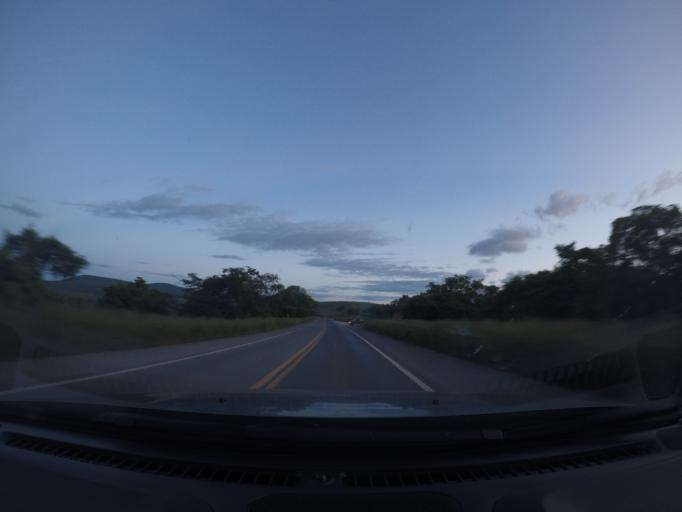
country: BR
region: Bahia
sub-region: Seabra
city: Seabra
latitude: -12.4838
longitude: -41.7372
